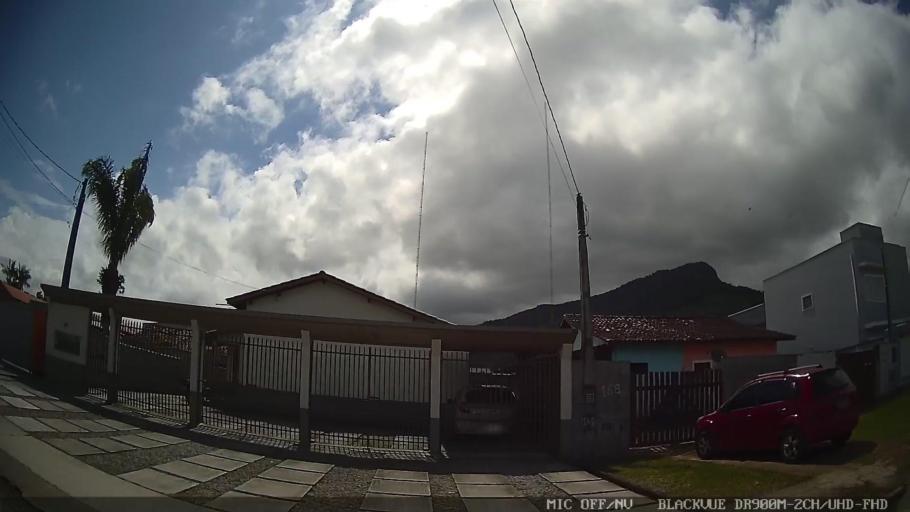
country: BR
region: Sao Paulo
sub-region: Caraguatatuba
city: Caraguatatuba
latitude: -23.6334
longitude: -45.4387
